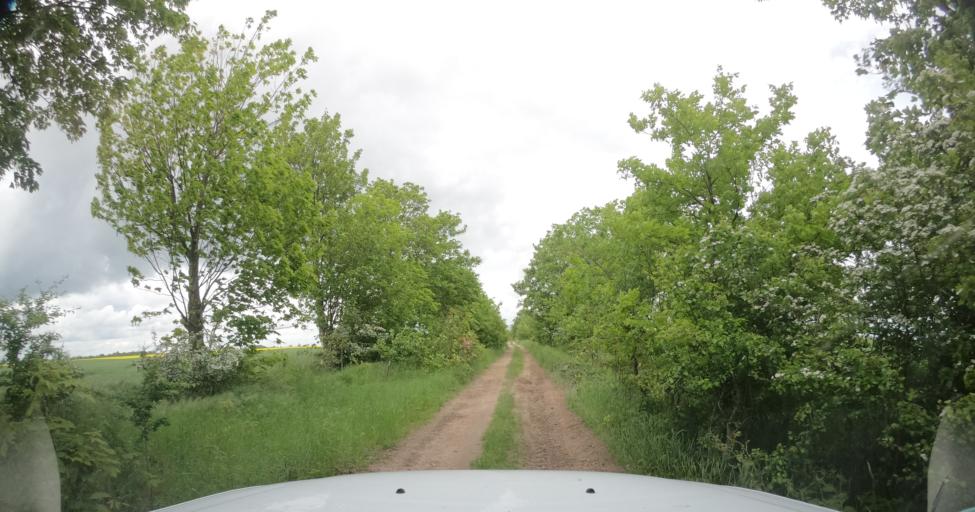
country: PL
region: West Pomeranian Voivodeship
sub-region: Powiat pyrzycki
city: Kozielice
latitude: 53.0848
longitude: 14.8252
